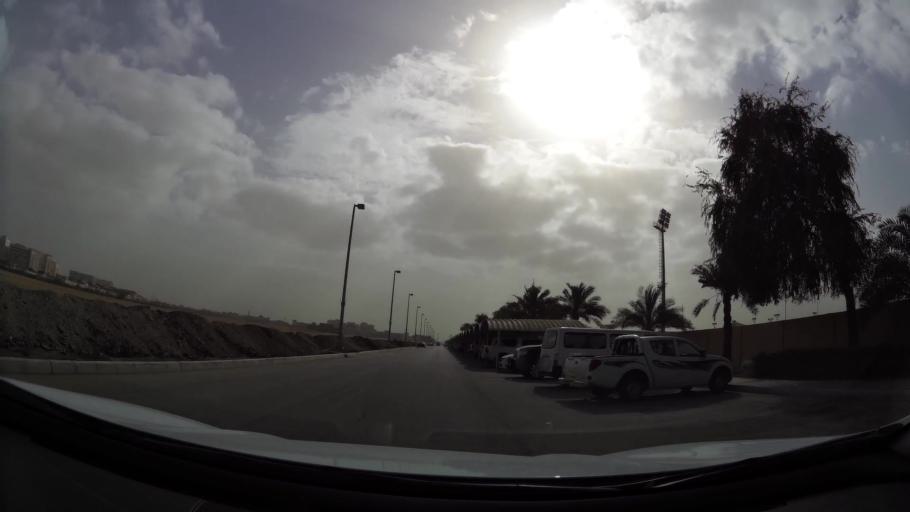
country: AE
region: Abu Dhabi
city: Abu Dhabi
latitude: 24.4077
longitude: 54.4806
